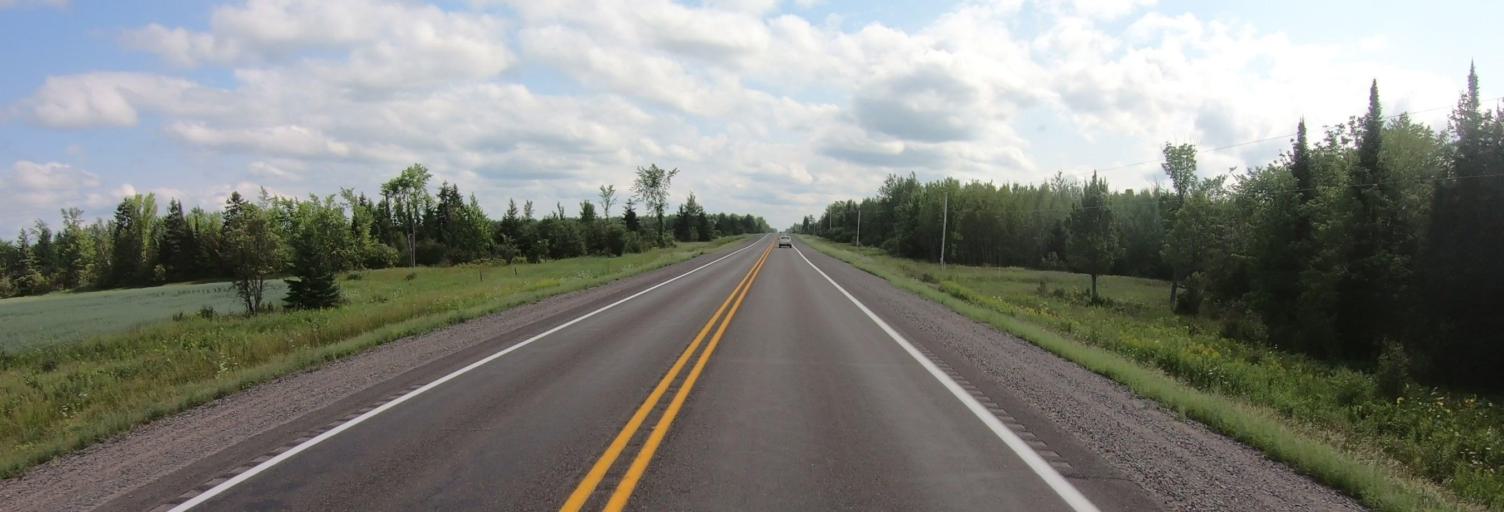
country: US
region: Michigan
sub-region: Ontonagon County
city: Ontonagon
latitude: 46.6047
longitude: -89.1784
